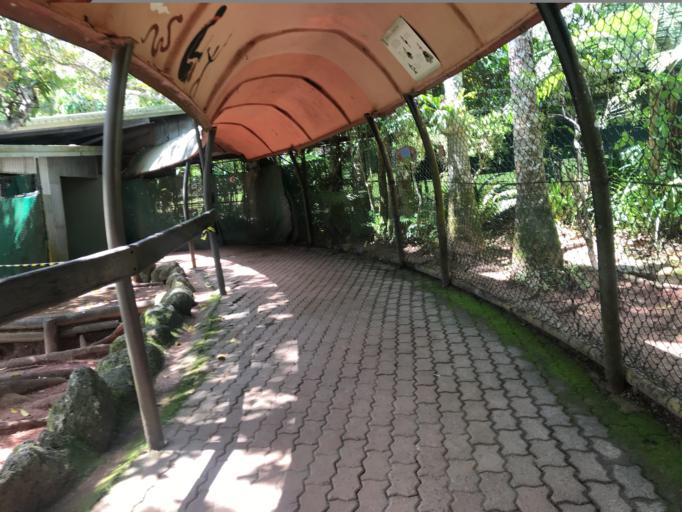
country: AU
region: Queensland
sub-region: Tablelands
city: Kuranda
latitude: -16.8234
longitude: 145.6523
